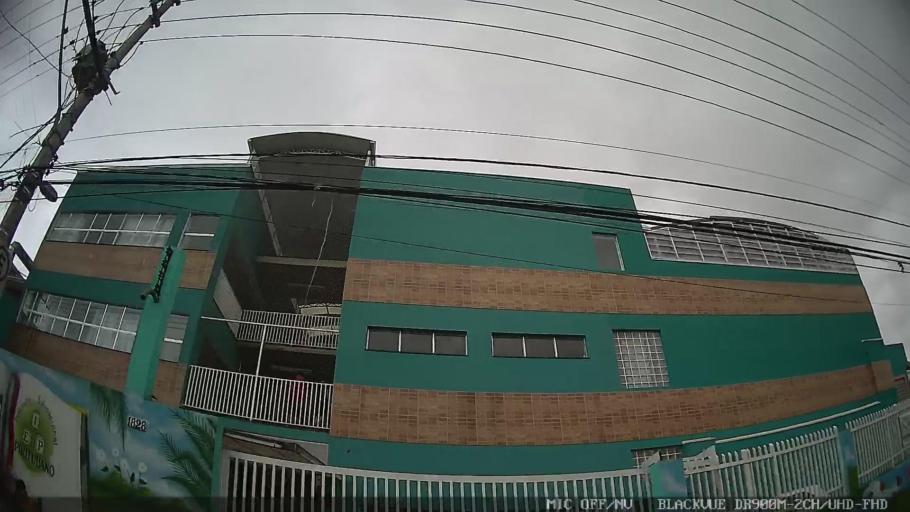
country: BR
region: Sao Paulo
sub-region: Osasco
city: Osasco
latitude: -23.4918
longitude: -46.7451
